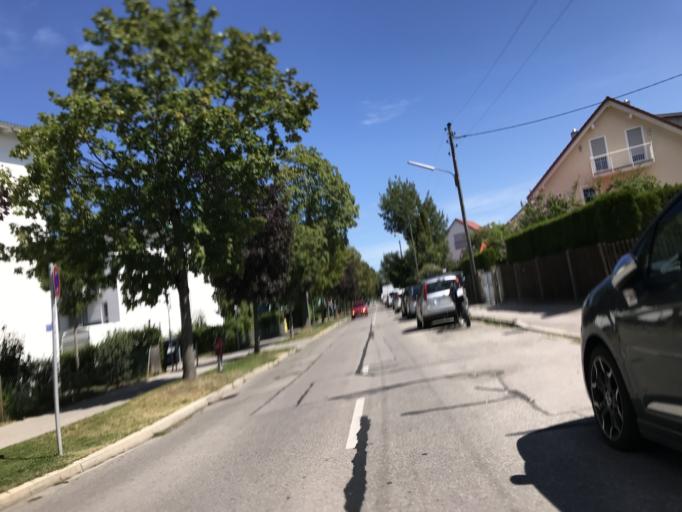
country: DE
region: Bavaria
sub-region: Upper Bavaria
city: Puchheim
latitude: 48.1753
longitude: 11.3522
